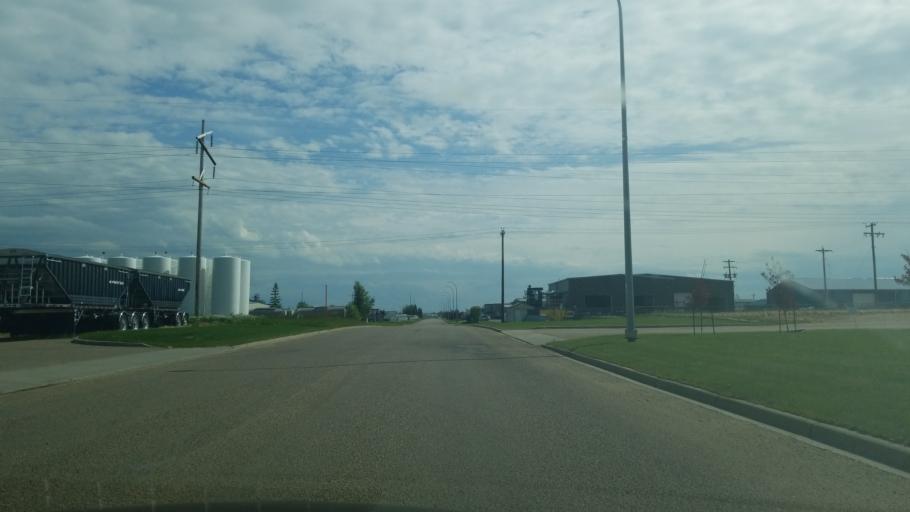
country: CA
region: Saskatchewan
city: Lloydminster
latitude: 53.2932
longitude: -110.0368
